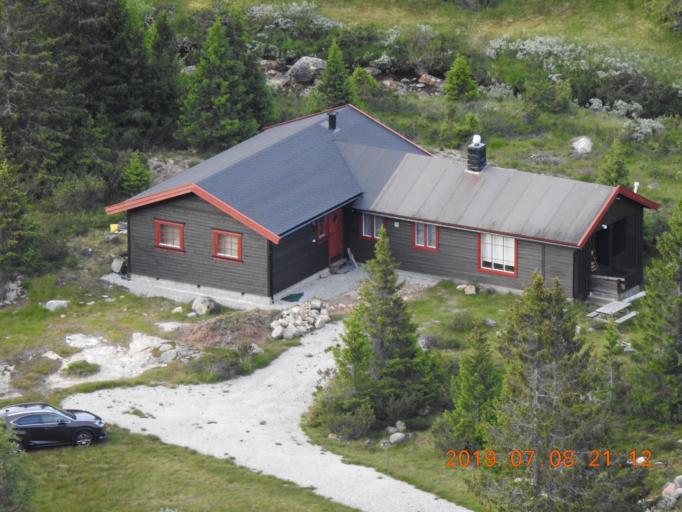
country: NO
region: Buskerud
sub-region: Nes
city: Nesbyen
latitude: 60.3587
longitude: 9.1820
